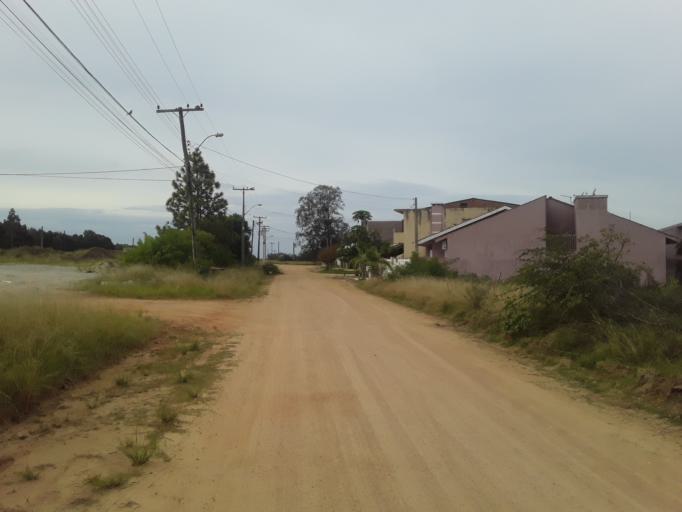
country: BR
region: Rio Grande do Sul
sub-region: Sao Lourenco Do Sul
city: Sao Lourenco do Sul
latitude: -31.3552
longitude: -51.9864
